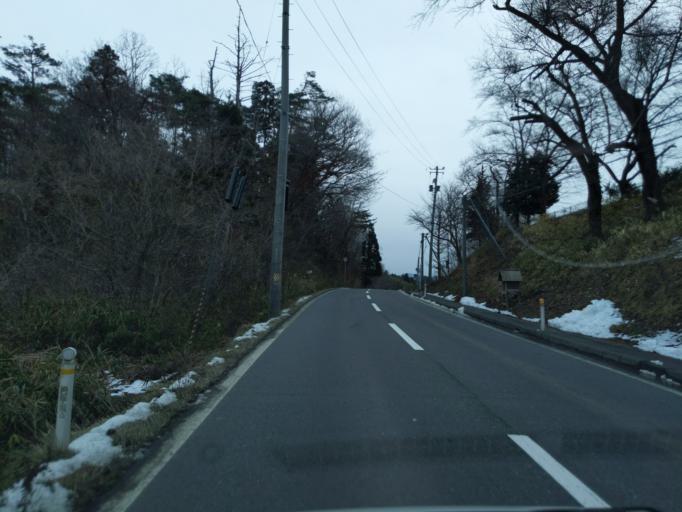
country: JP
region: Iwate
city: Mizusawa
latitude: 39.1553
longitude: 141.2107
